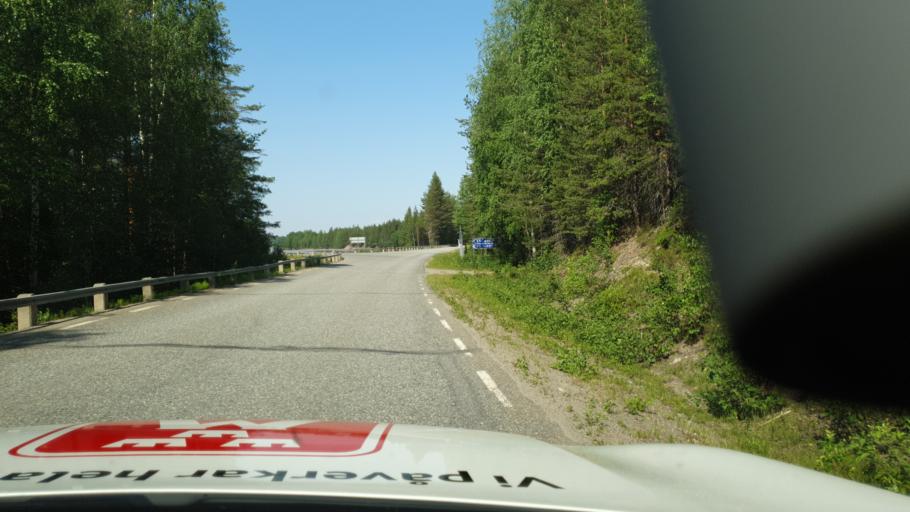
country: SE
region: Vaesterbotten
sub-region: Skelleftea Kommun
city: Langsele
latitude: 64.9622
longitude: 19.8912
